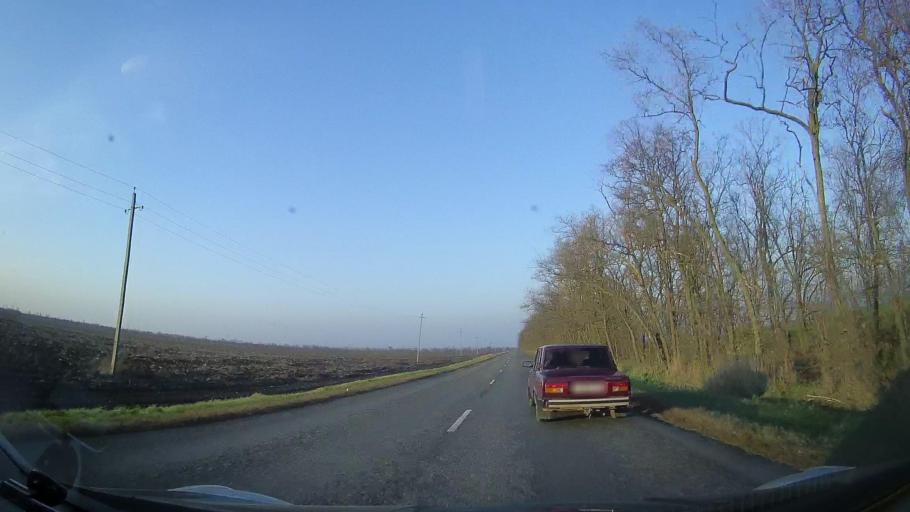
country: RU
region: Rostov
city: Ol'ginskaya
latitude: 47.0901
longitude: 39.9776
